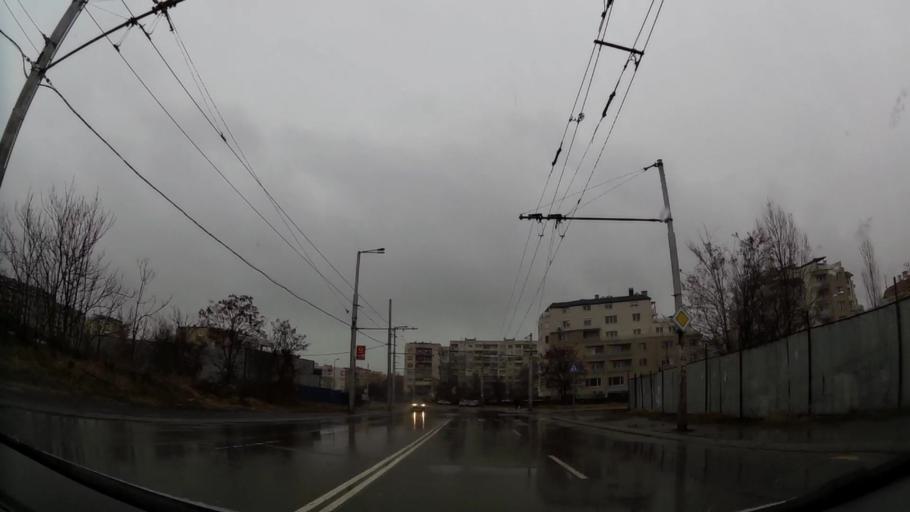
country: BG
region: Sofia-Capital
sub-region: Stolichna Obshtina
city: Sofia
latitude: 42.6463
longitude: 23.4048
